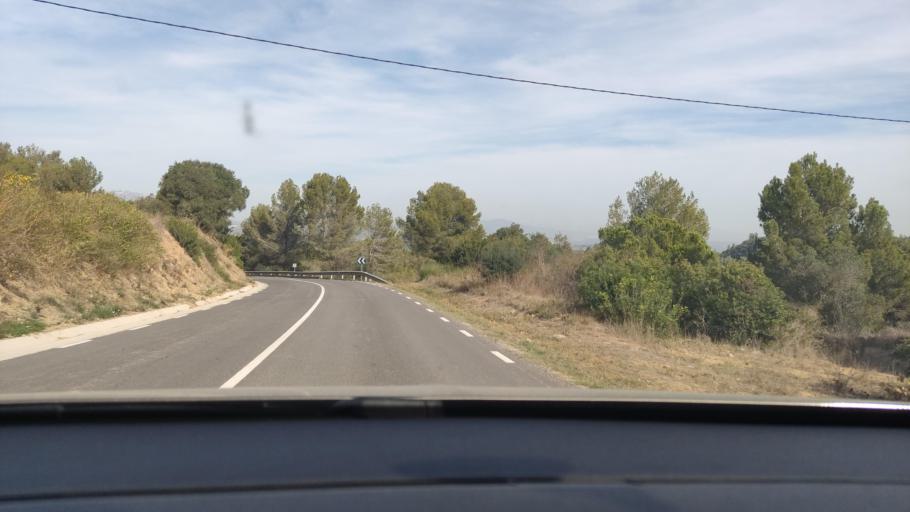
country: ES
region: Catalonia
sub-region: Provincia de Barcelona
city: Sant Sadurni d'Anoia
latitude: 41.4112
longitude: 1.8006
